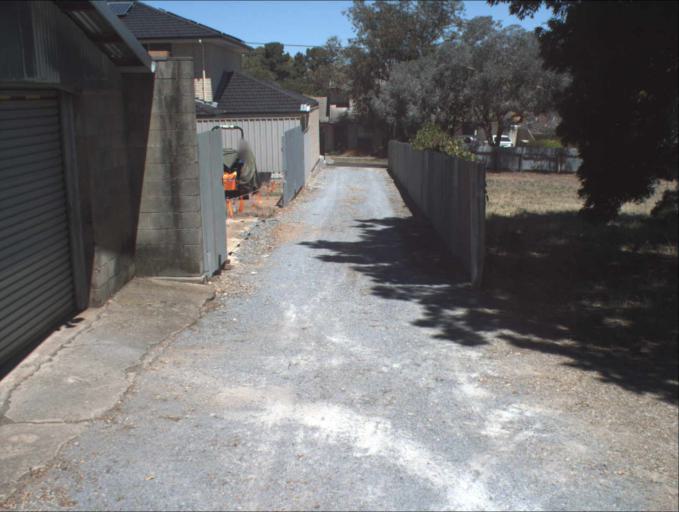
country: AU
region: South Australia
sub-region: Port Adelaide Enfield
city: Blair Athol
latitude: -34.8621
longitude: 138.6056
